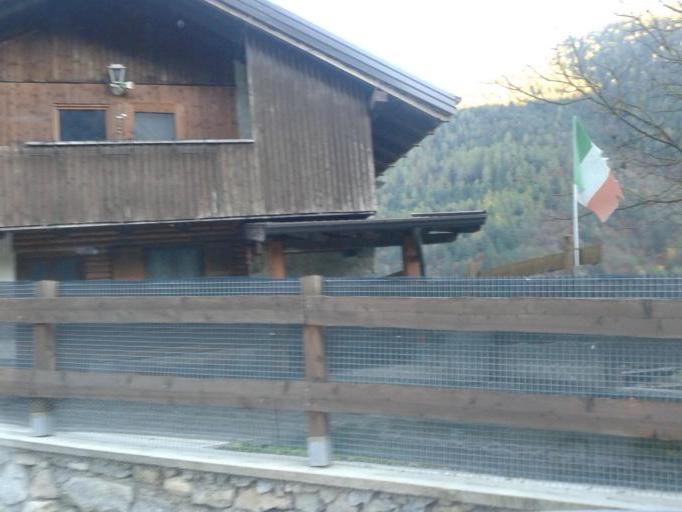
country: IT
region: Trentino-Alto Adige
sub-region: Provincia di Trento
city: Pieve di Ledro
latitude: 45.8945
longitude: 10.7039
